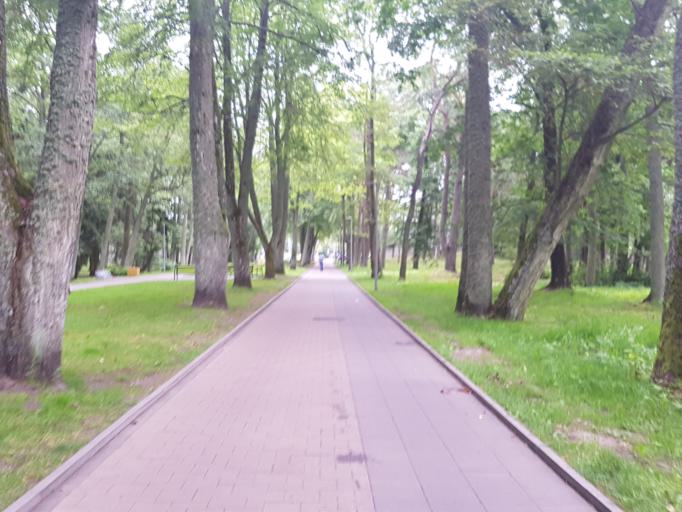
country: LT
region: Klaipedos apskritis
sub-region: Klaipeda
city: Palanga
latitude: 55.9177
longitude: 21.0525
